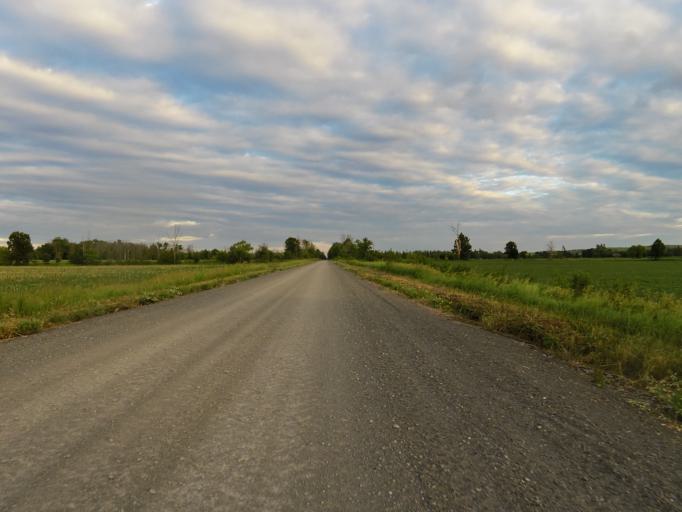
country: CA
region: Ontario
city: Arnprior
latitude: 45.3453
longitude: -76.3006
